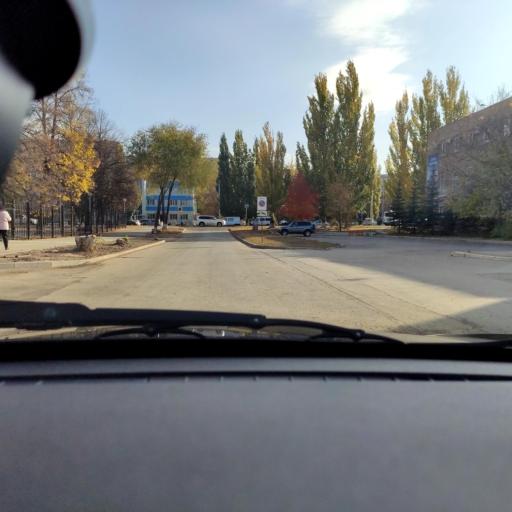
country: RU
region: Samara
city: Tol'yatti
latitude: 53.5167
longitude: 49.2842
